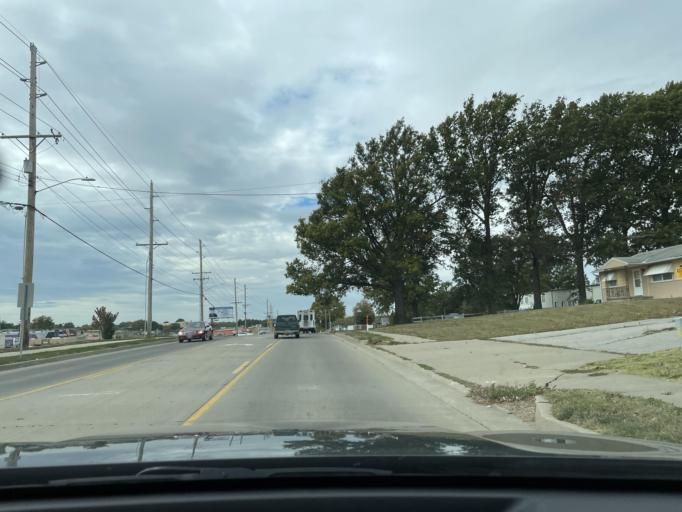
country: US
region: Missouri
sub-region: Buchanan County
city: Saint Joseph
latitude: 39.7698
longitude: -94.7992
